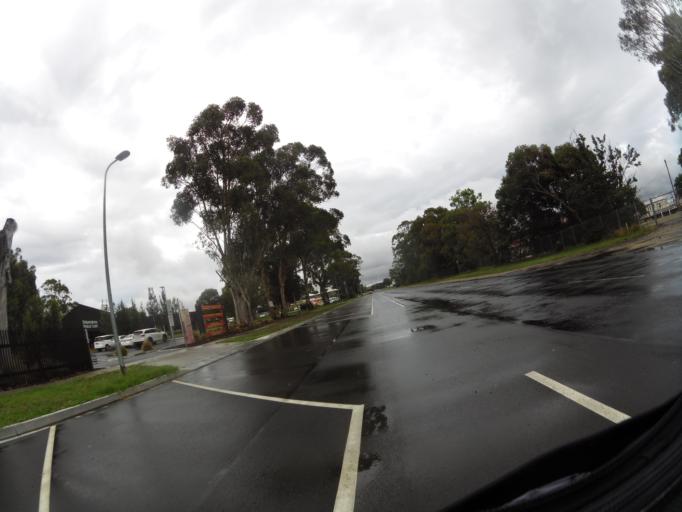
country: AU
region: Victoria
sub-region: East Gippsland
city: Bairnsdale
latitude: -37.8293
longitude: 147.6288
